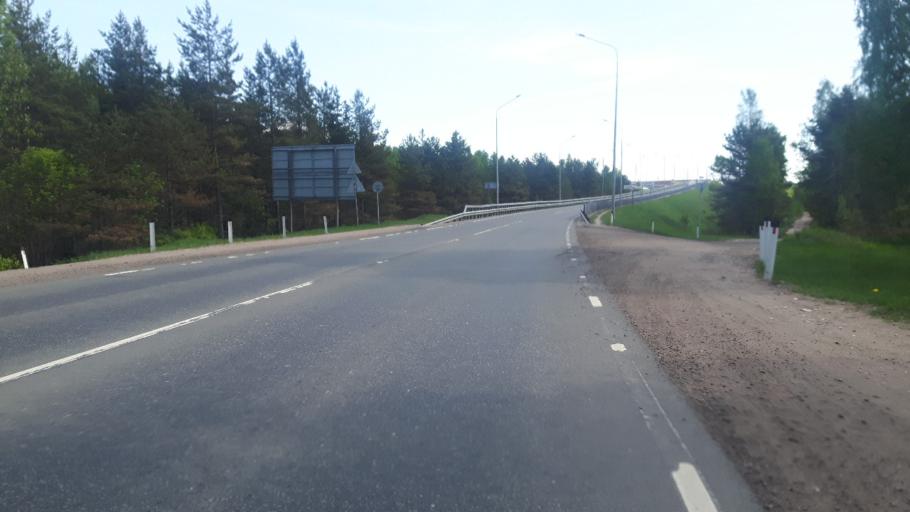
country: RU
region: Leningrad
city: Vyborg
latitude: 60.7429
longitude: 28.6807
